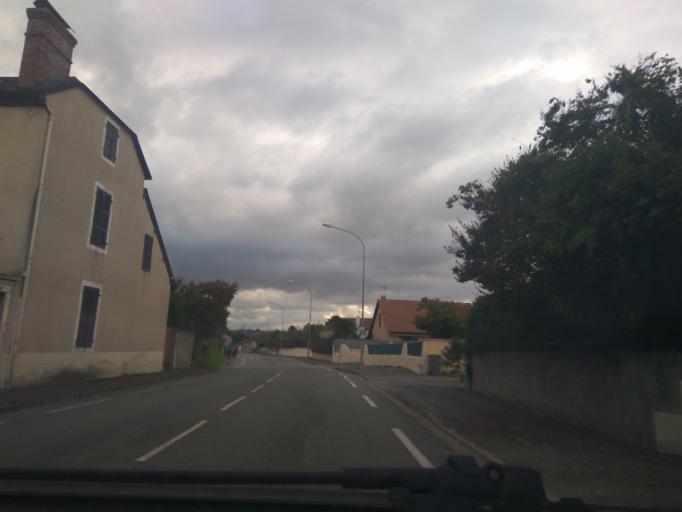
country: FR
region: Aquitaine
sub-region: Departement des Pyrenees-Atlantiques
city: Bizanos
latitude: 43.2894
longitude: -0.3414
